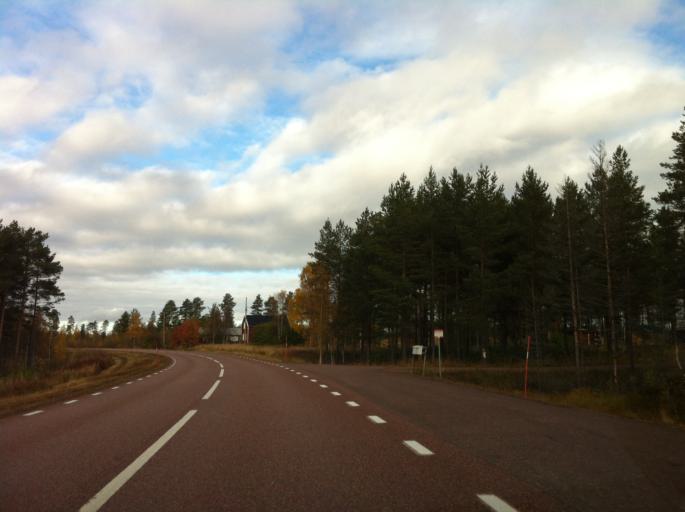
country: SE
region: Dalarna
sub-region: Alvdalens Kommun
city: AElvdalen
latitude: 61.5301
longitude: 13.3580
